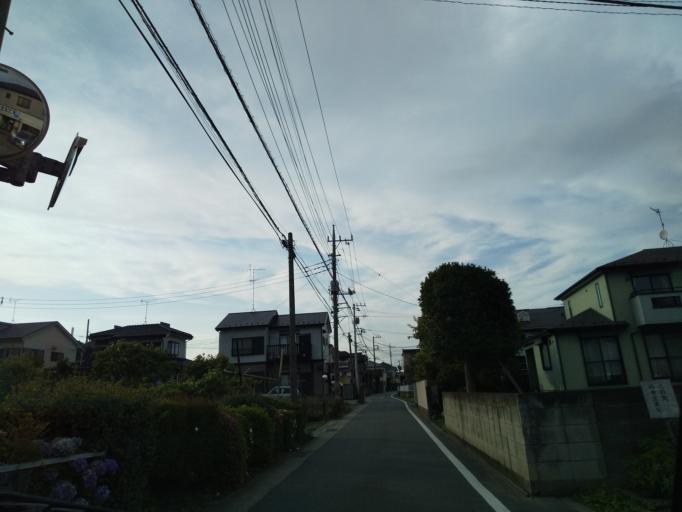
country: JP
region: Kanagawa
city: Zama
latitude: 35.5056
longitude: 139.3621
